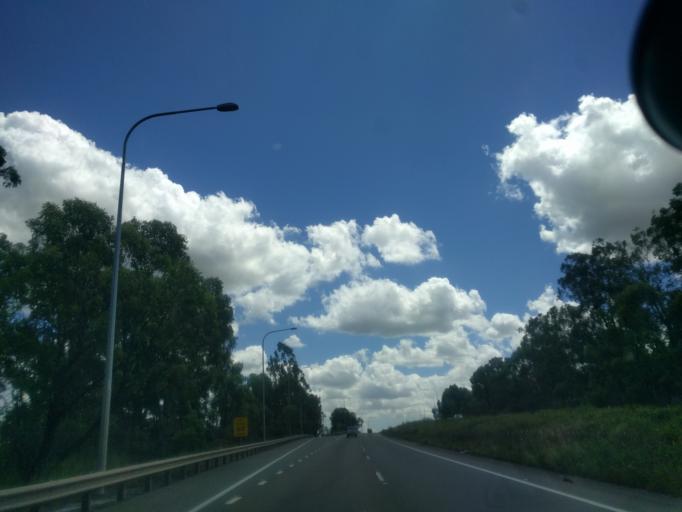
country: AU
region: Queensland
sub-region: Ipswich
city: Riverview
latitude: -27.6024
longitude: 152.8318
